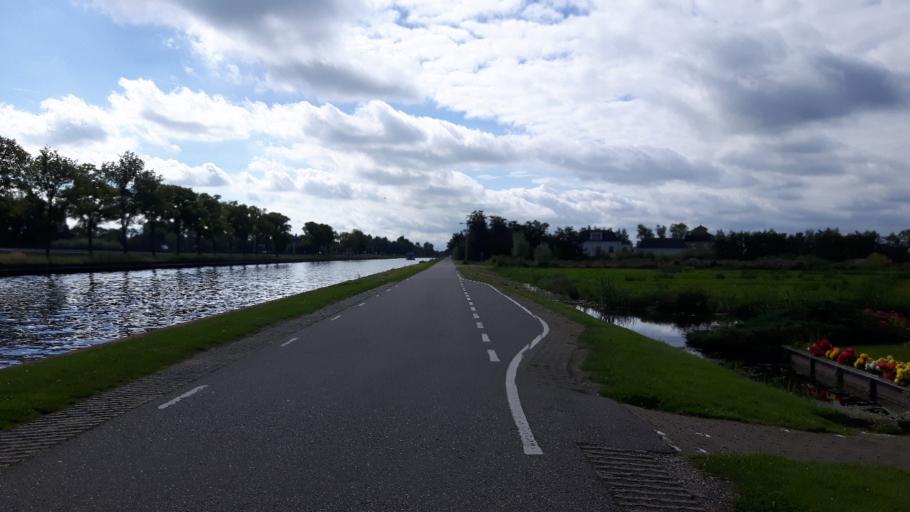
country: NL
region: North Holland
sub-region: Gemeente Landsmeer
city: Landsmeer
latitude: 52.4427
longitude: 4.9494
